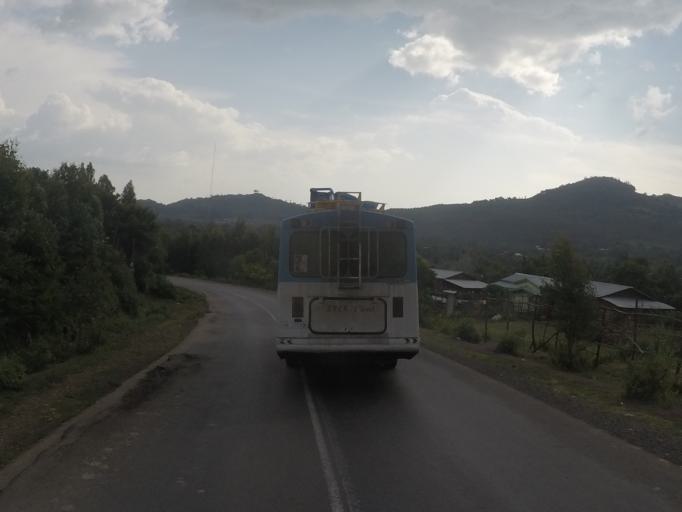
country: ET
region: Amhara
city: Gondar
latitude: 12.6503
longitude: 37.4854
